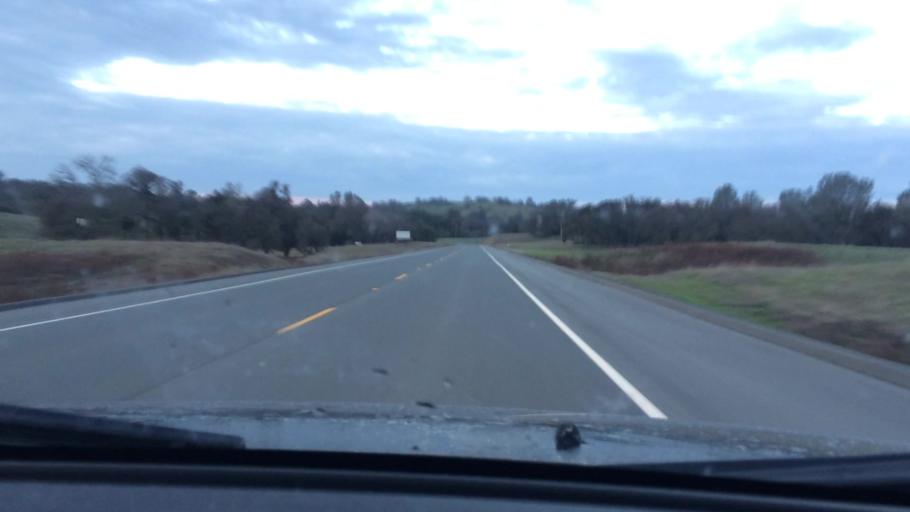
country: US
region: California
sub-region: Amador County
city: Ione
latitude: 38.3935
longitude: -120.9016
